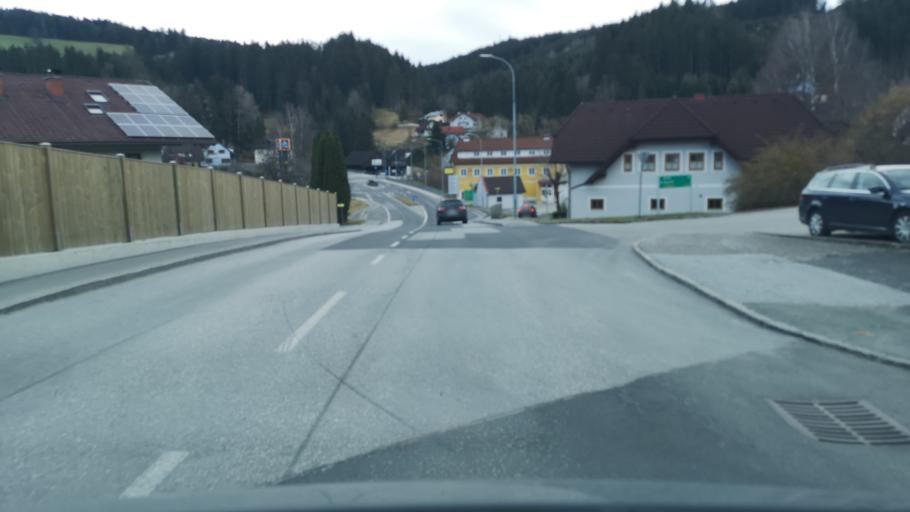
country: AT
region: Styria
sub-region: Politischer Bezirk Weiz
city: Birkfeld
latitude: 47.3540
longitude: 15.6989
